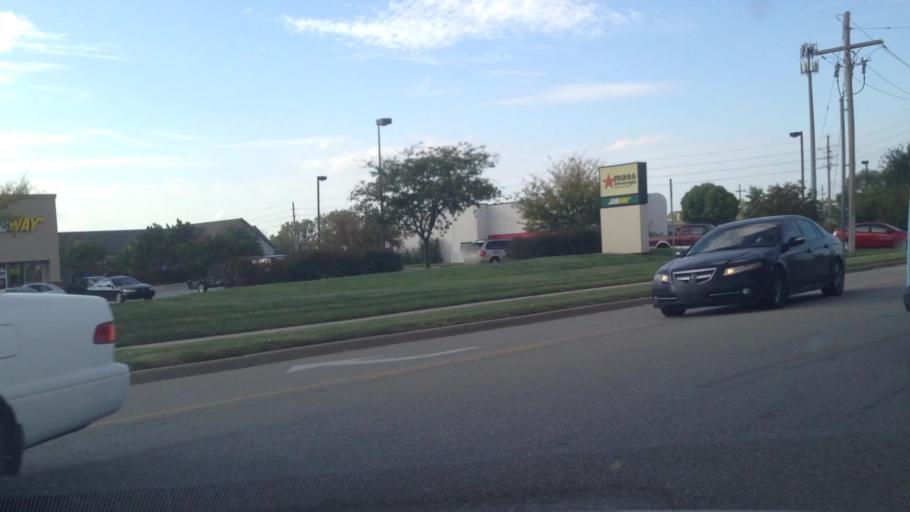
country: US
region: Kansas
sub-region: Douglas County
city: Lawrence
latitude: 38.9268
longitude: -95.2626
